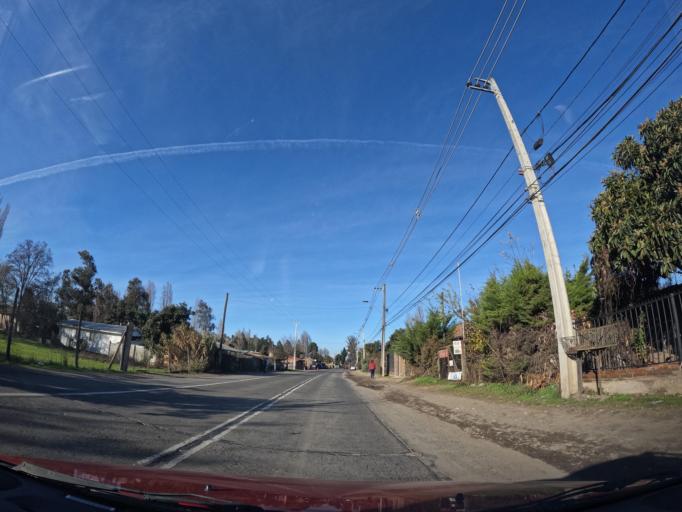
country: CL
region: Maule
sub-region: Provincia de Linares
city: San Javier
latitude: -35.5719
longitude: -71.6873
